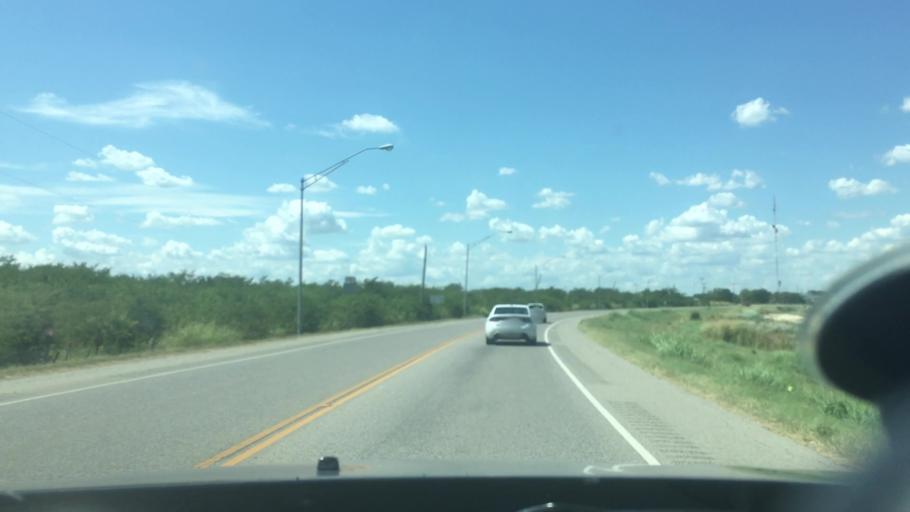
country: US
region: Oklahoma
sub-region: Marshall County
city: Madill
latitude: 34.0655
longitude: -96.7618
